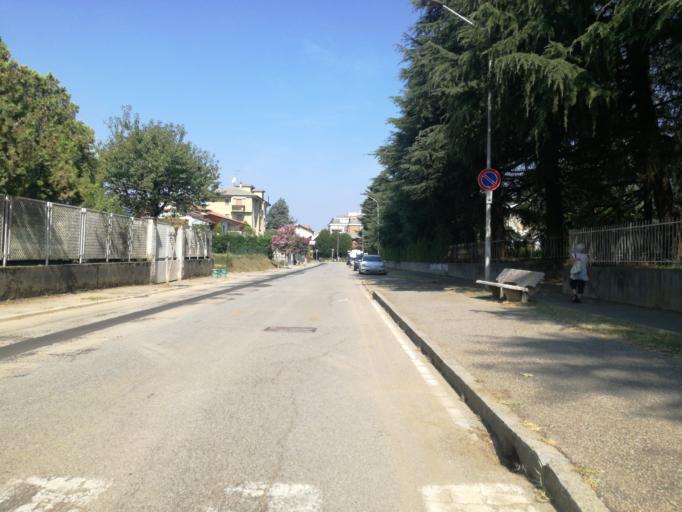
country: IT
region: Lombardy
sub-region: Provincia di Monza e Brianza
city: Cornate d'Adda
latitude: 45.6297
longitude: 9.4744
